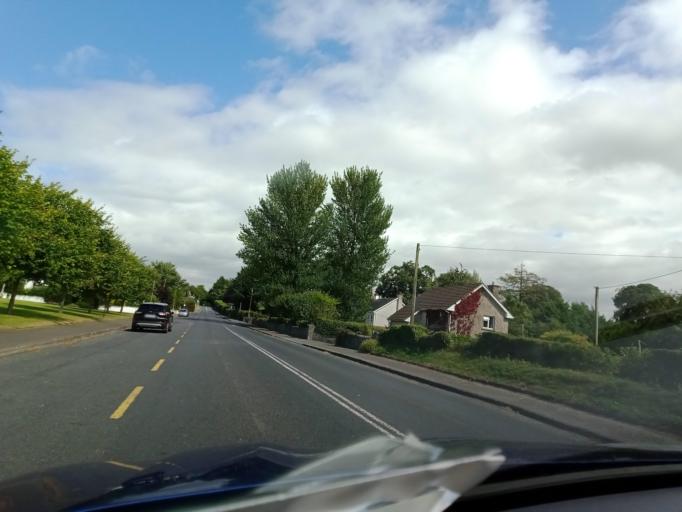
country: IE
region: Leinster
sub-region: Laois
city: Abbeyleix
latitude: 52.9201
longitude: -7.3414
